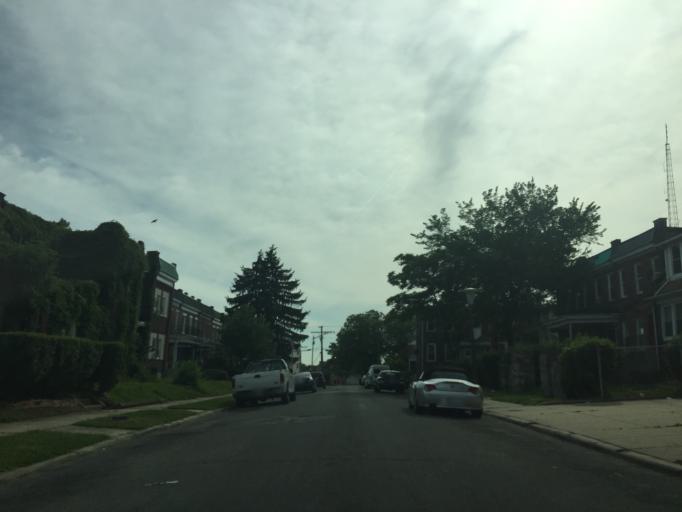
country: US
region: Maryland
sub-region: Baltimore County
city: Lochearn
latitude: 39.3377
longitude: -76.6618
